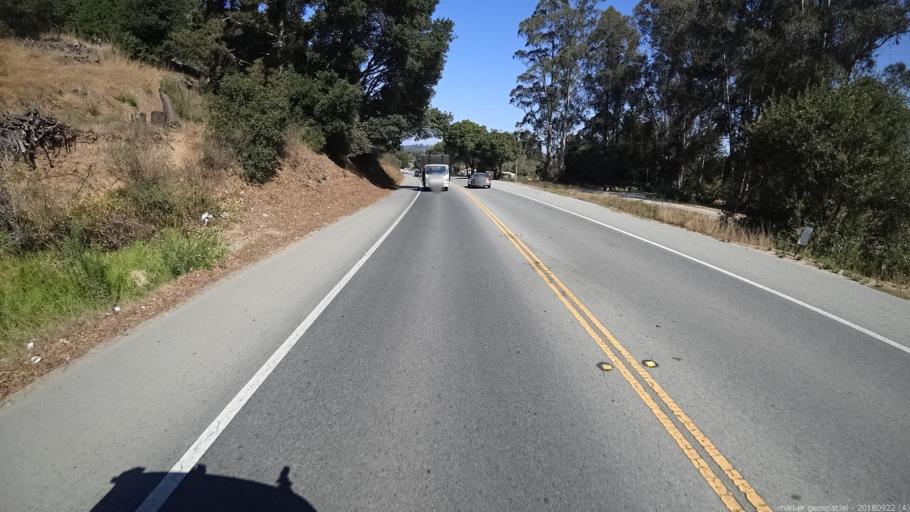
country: US
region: California
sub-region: Monterey County
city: Las Lomas
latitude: 36.8516
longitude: -121.6902
